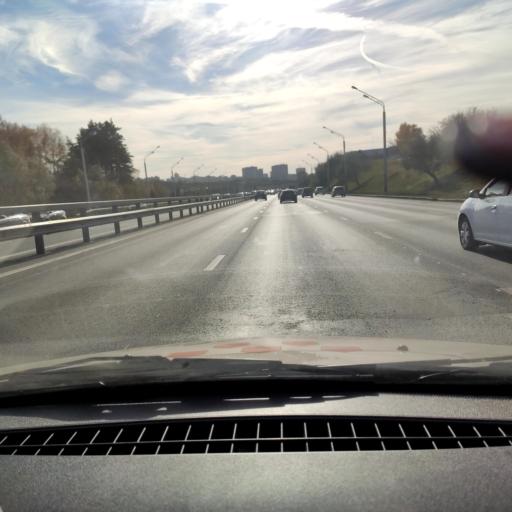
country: RU
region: Bashkortostan
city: Ufa
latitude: 54.7416
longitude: 56.0104
